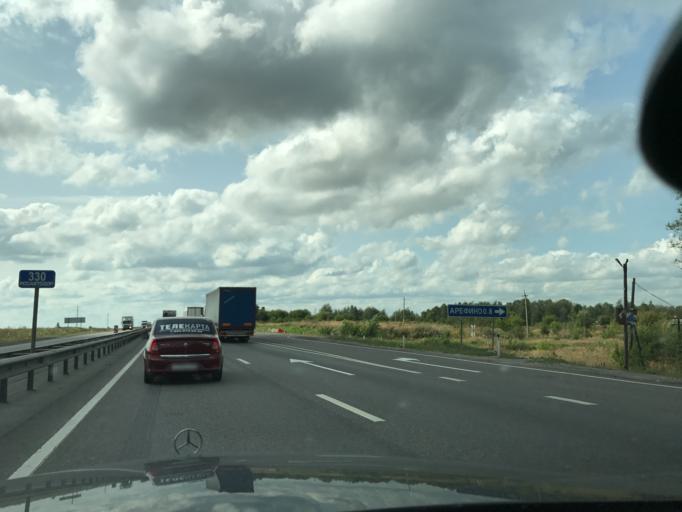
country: RU
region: Vladimir
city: Gorokhovets
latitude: 56.1705
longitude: 42.6383
